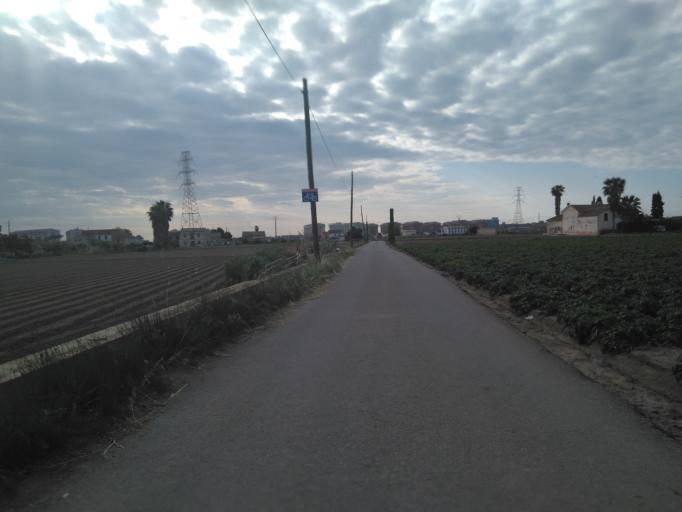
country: ES
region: Valencia
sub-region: Provincia de Valencia
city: Alboraya
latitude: 39.4942
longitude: -0.3409
